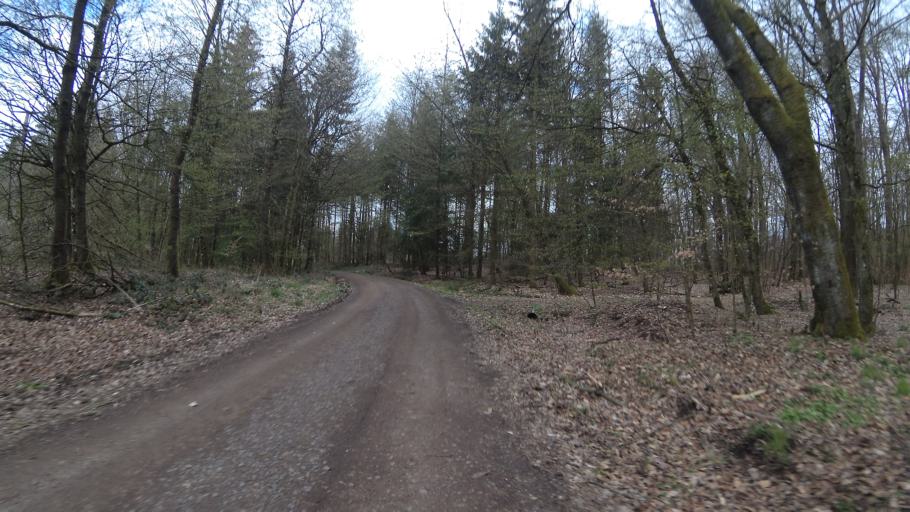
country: DE
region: Saarland
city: Oberthal
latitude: 49.4806
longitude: 7.0913
